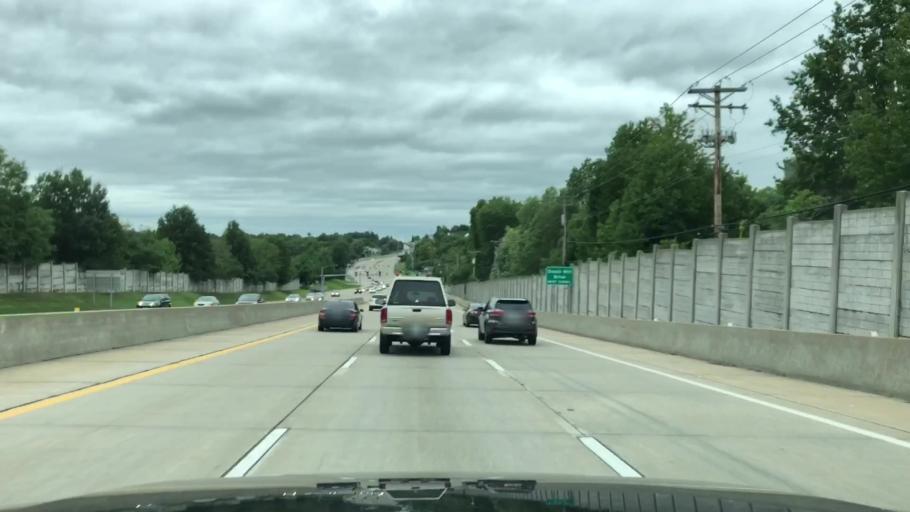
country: US
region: Missouri
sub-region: Saint Louis County
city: Manchester
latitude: 38.6138
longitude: -90.5123
